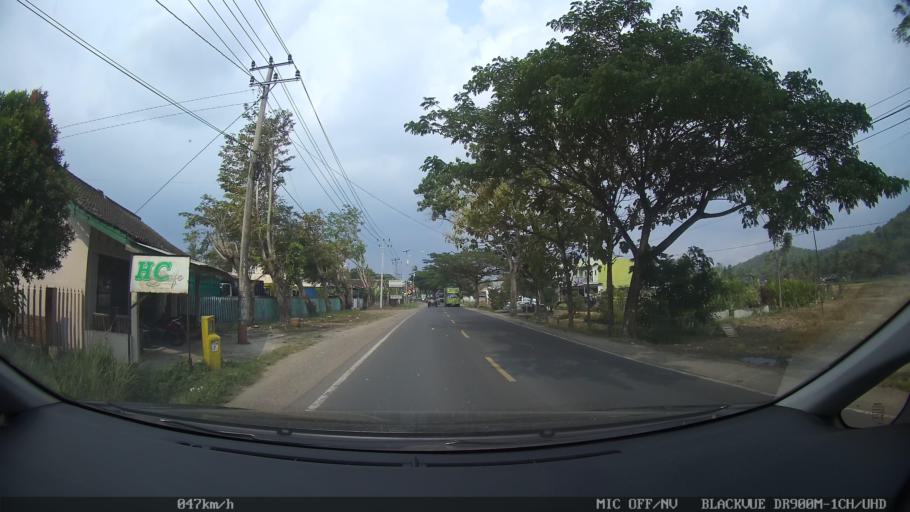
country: ID
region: Lampung
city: Gadingrejo
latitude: -5.3804
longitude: 105.0270
